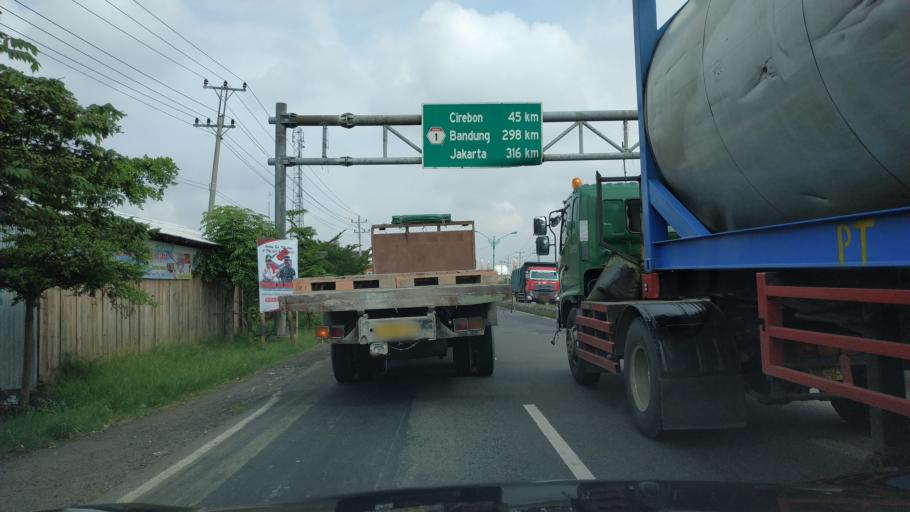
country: ID
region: Central Java
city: Bulakamba
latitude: -6.8748
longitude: 108.9265
